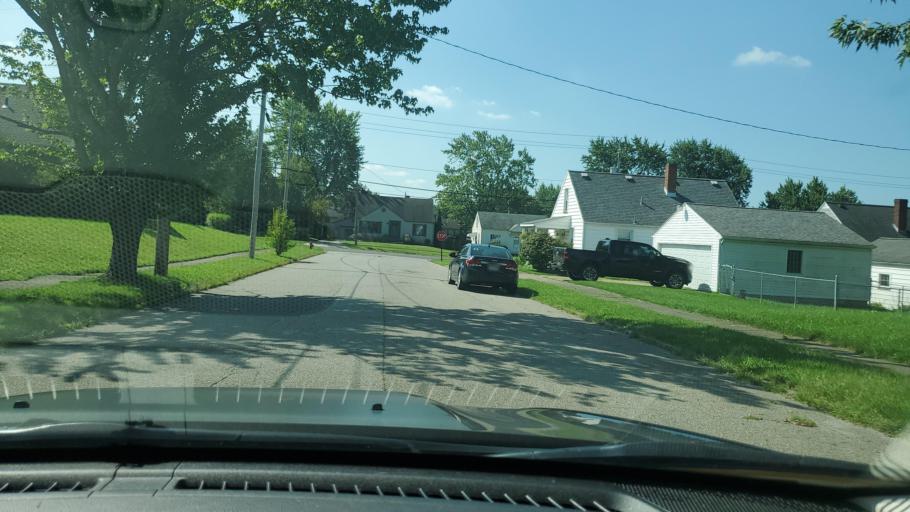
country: US
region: Ohio
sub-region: Trumbull County
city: Girard
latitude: 41.1627
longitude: -80.6931
